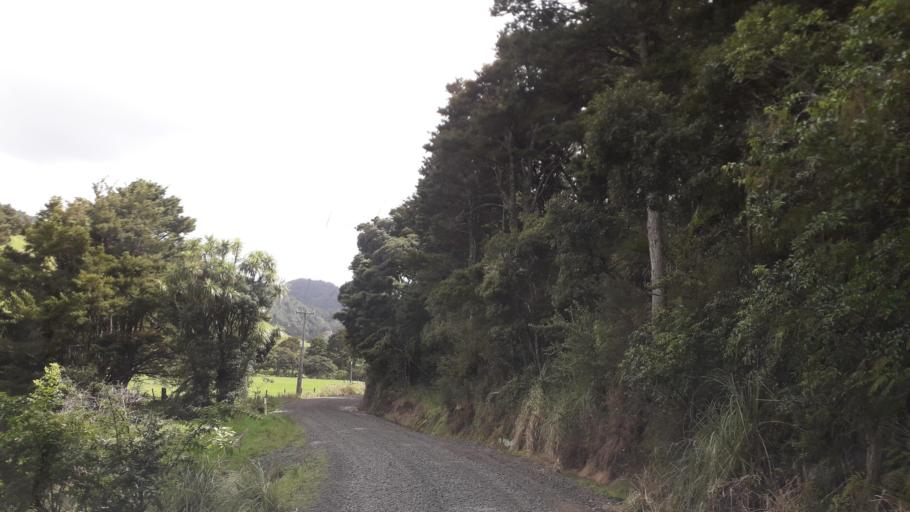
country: NZ
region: Northland
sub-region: Far North District
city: Ahipara
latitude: -35.2362
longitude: 173.2650
